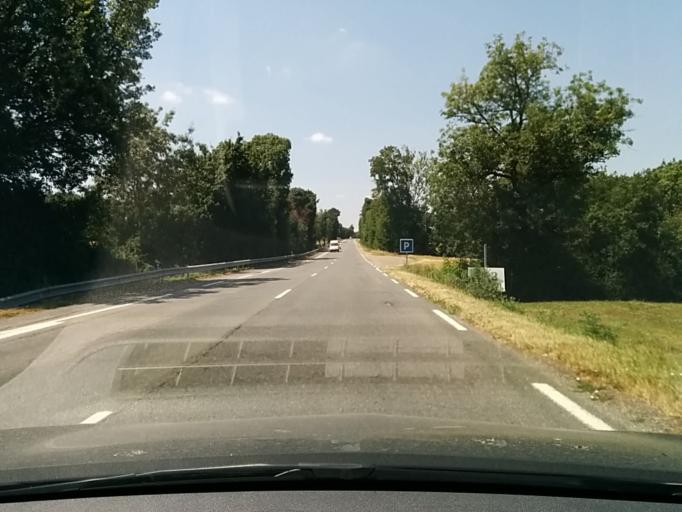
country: FR
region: Midi-Pyrenees
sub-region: Departement du Gers
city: Pujaudran
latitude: 43.6025
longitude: 1.0174
